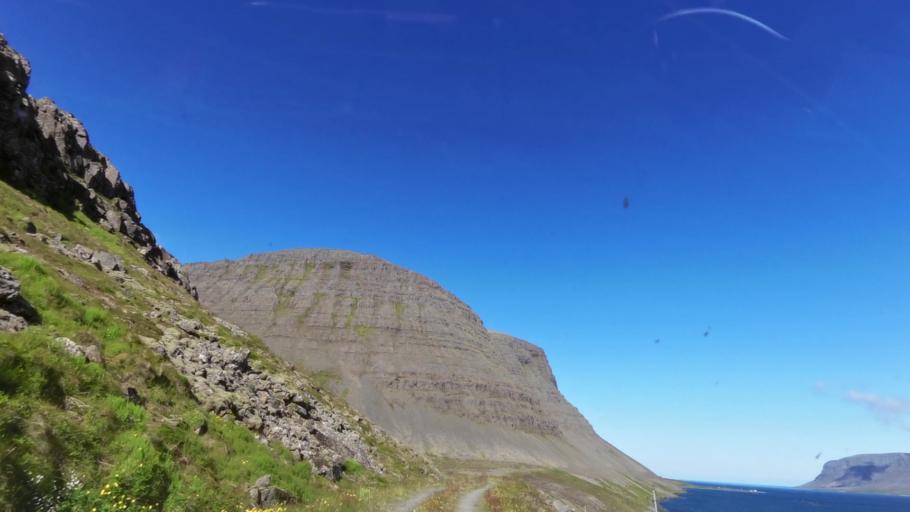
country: IS
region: West
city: Olafsvik
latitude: 65.6244
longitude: -23.8893
